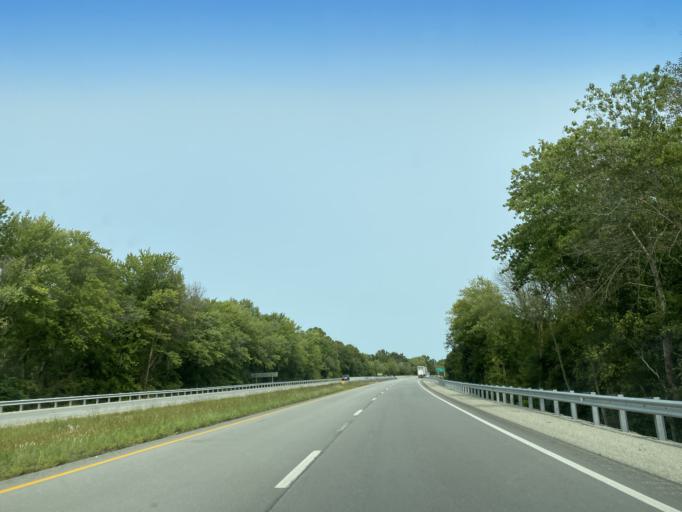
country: US
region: Kentucky
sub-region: Bullitt County
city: Lebanon Junction
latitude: 37.7458
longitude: -85.6858
